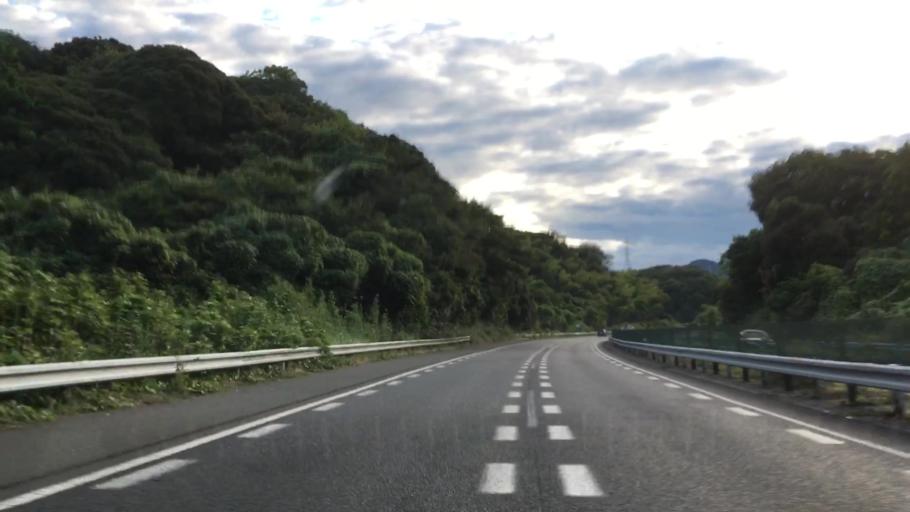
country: JP
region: Yamaguchi
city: Shimonoseki
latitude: 34.0457
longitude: 130.9974
